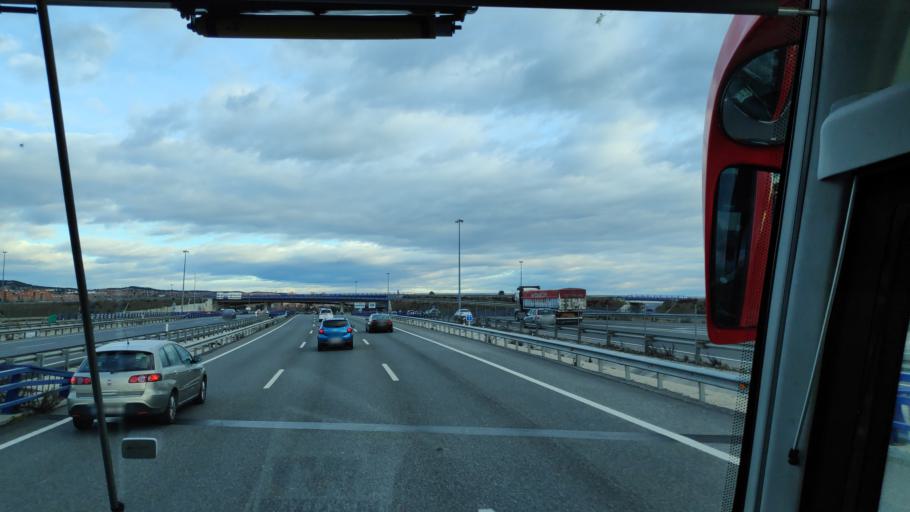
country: ES
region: Madrid
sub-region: Provincia de Madrid
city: Villa de Vallecas
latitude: 40.3604
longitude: -3.5670
